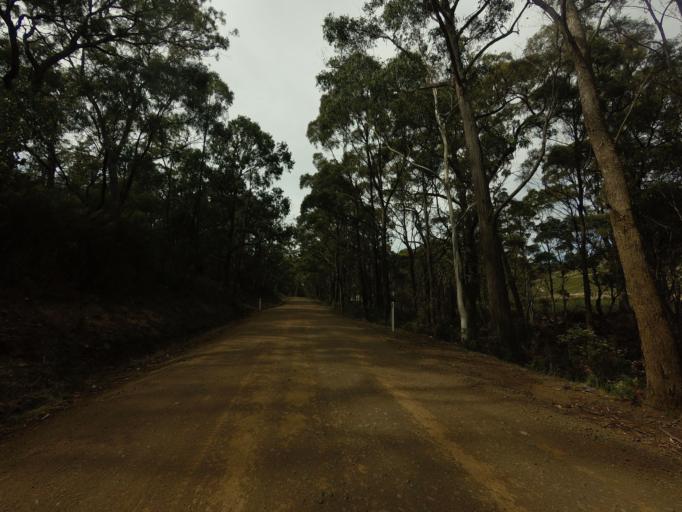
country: AU
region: Tasmania
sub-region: Sorell
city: Sorell
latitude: -42.4821
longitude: 147.6148
